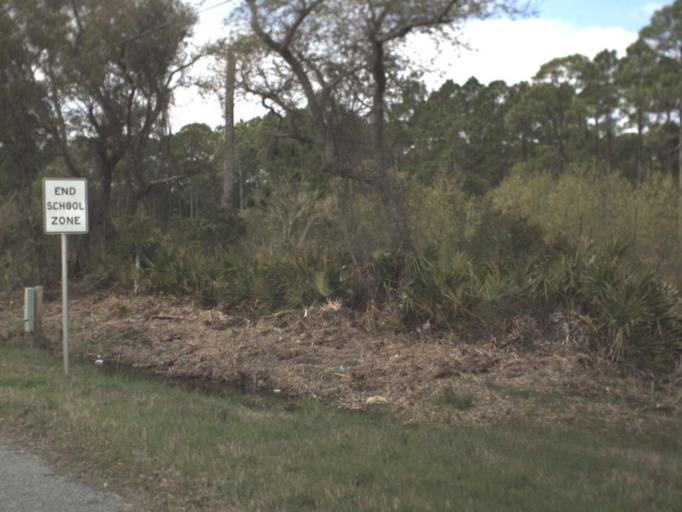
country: US
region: Florida
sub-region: Franklin County
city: Eastpoint
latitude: 29.7614
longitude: -84.8179
